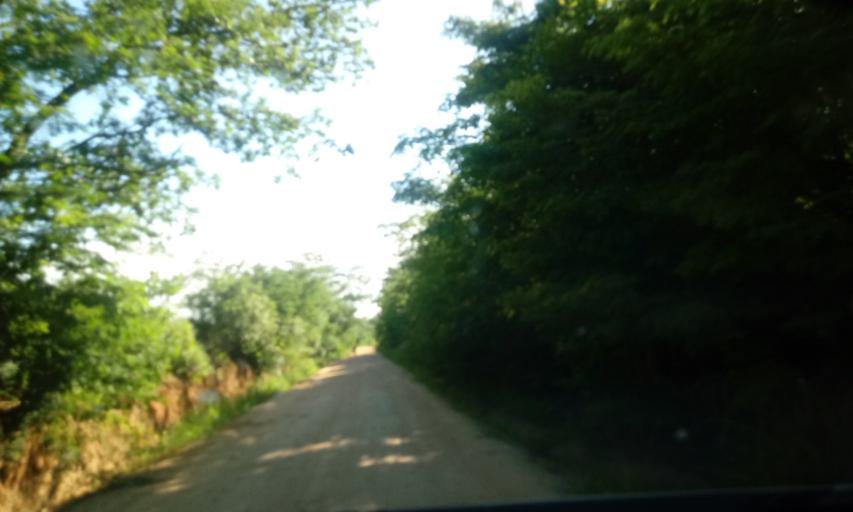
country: BR
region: Bahia
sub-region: Riacho De Santana
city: Riacho de Santana
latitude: -13.7877
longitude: -42.7275
